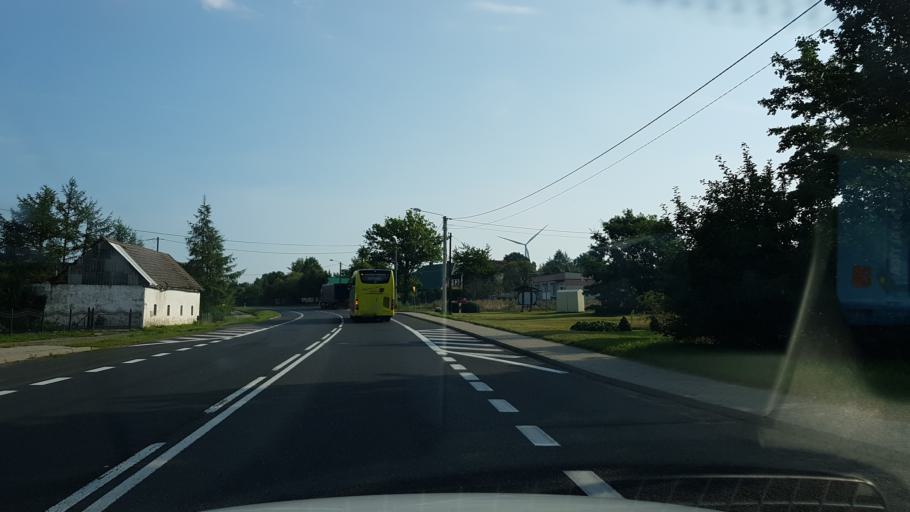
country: PL
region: West Pomeranian Voivodeship
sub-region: Powiat koszalinski
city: Sianow
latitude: 54.2700
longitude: 16.4243
